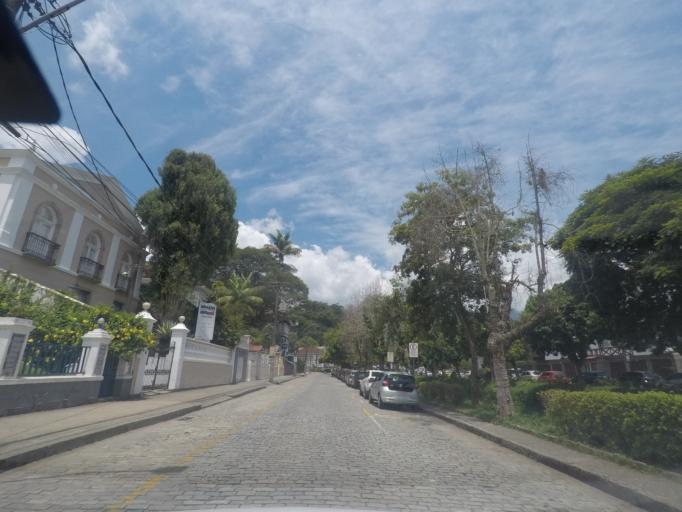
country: BR
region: Rio de Janeiro
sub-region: Petropolis
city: Petropolis
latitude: -22.5062
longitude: -43.1787
